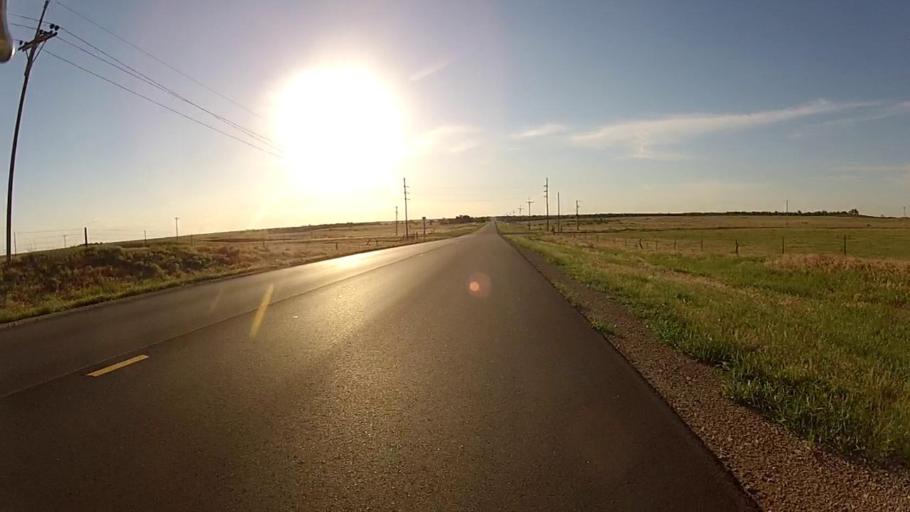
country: US
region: Kansas
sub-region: Comanche County
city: Coldwater
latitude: 37.2811
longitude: -99.2204
